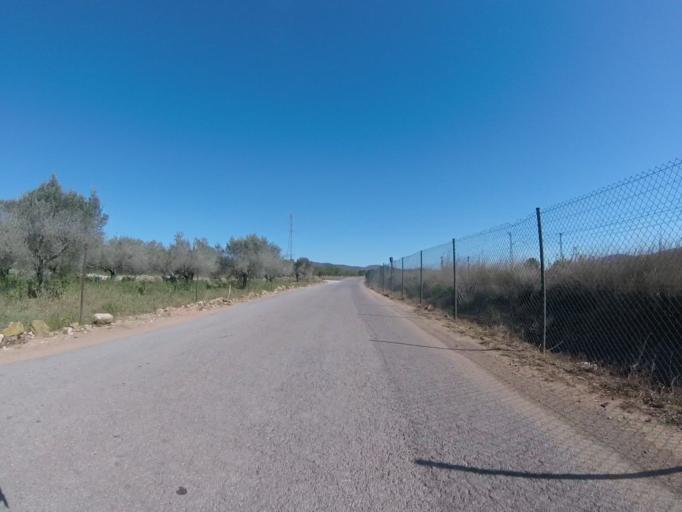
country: ES
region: Valencia
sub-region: Provincia de Castello
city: Alcala de Xivert
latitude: 40.3181
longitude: 0.2340
